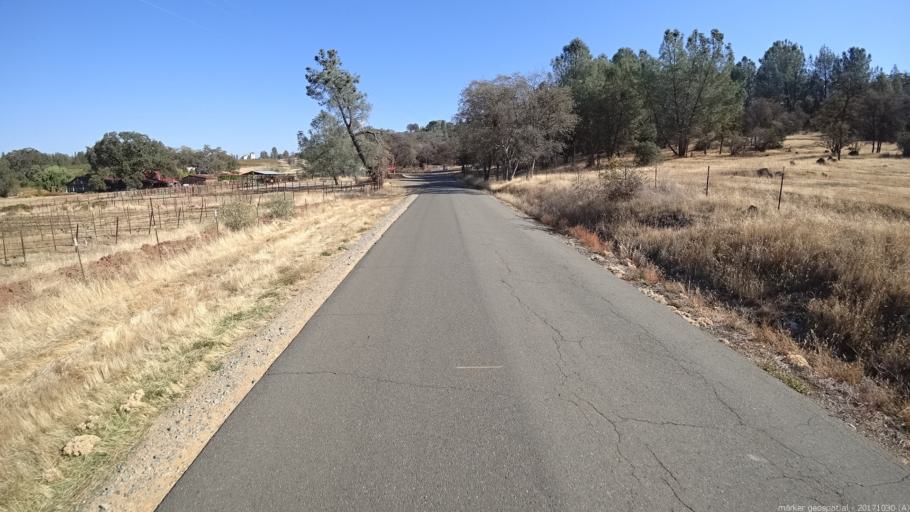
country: US
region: California
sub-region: Shasta County
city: Shingletown
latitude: 40.5095
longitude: -121.9851
